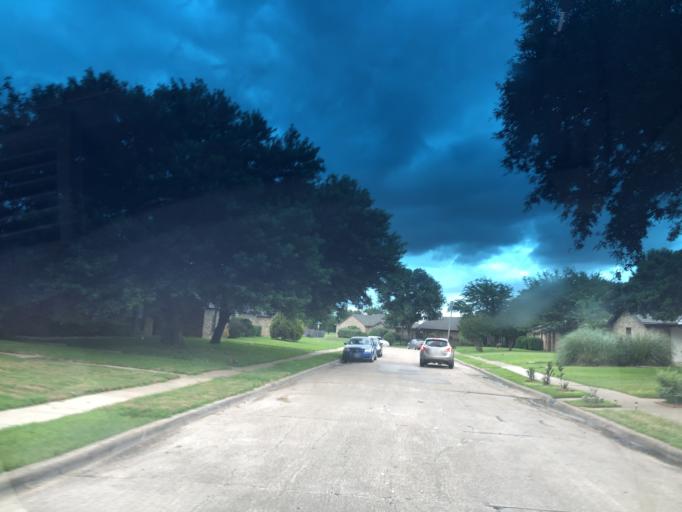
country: US
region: Texas
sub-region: Dallas County
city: Grand Prairie
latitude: 32.6990
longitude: -97.0042
